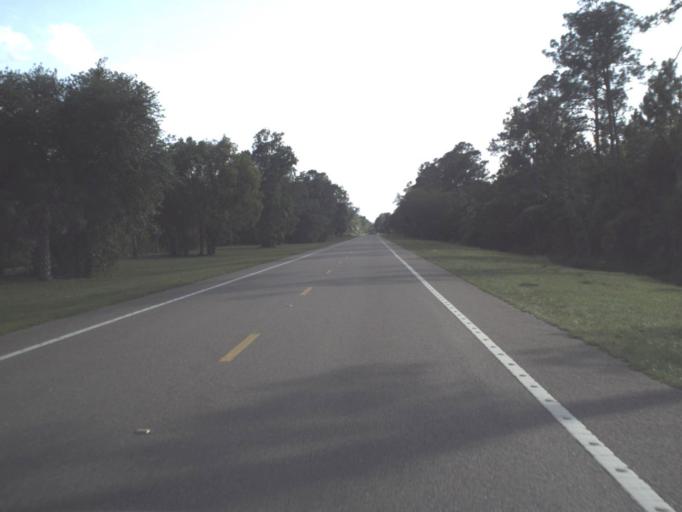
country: US
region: Florida
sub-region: Flagler County
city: Bunnell
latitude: 29.4561
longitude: -81.2667
